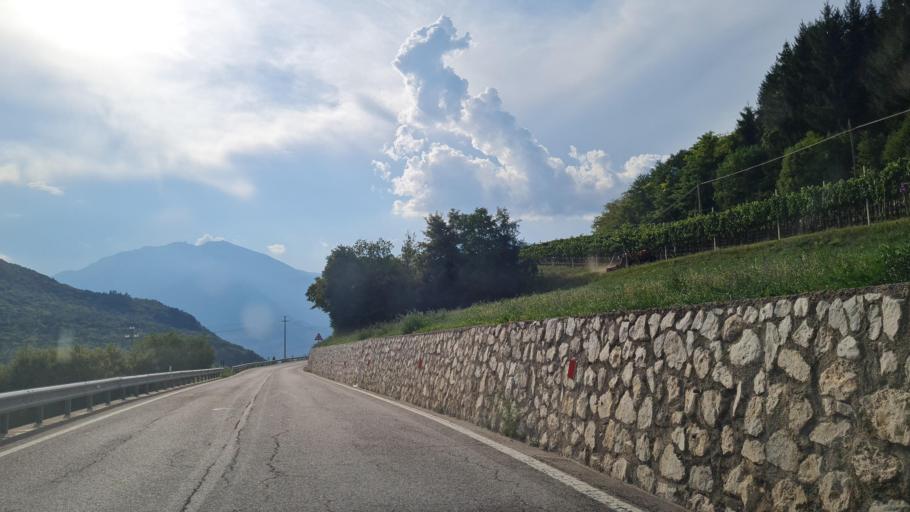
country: IT
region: Trentino-Alto Adige
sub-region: Provincia di Trento
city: Vigolo Vattaro
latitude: 46.0058
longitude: 11.1761
